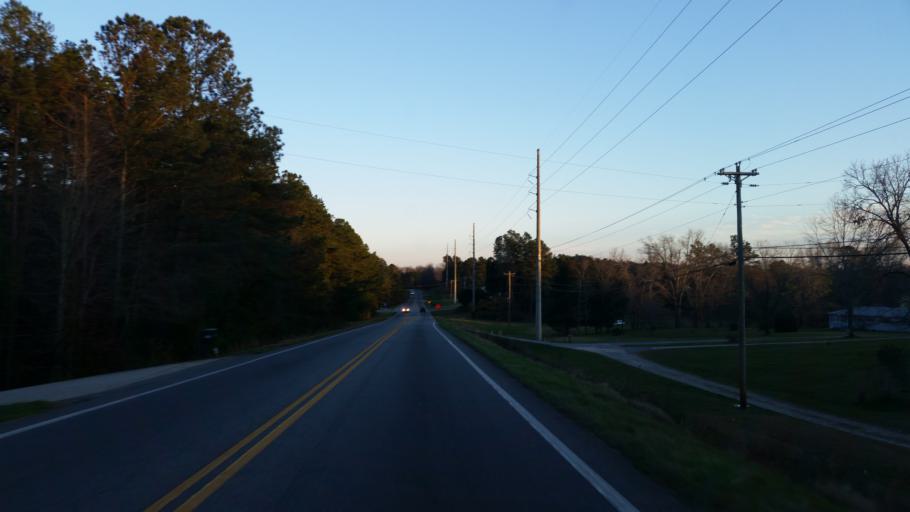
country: US
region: Georgia
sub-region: Hall County
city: Oakwood
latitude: 34.3187
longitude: -84.0023
